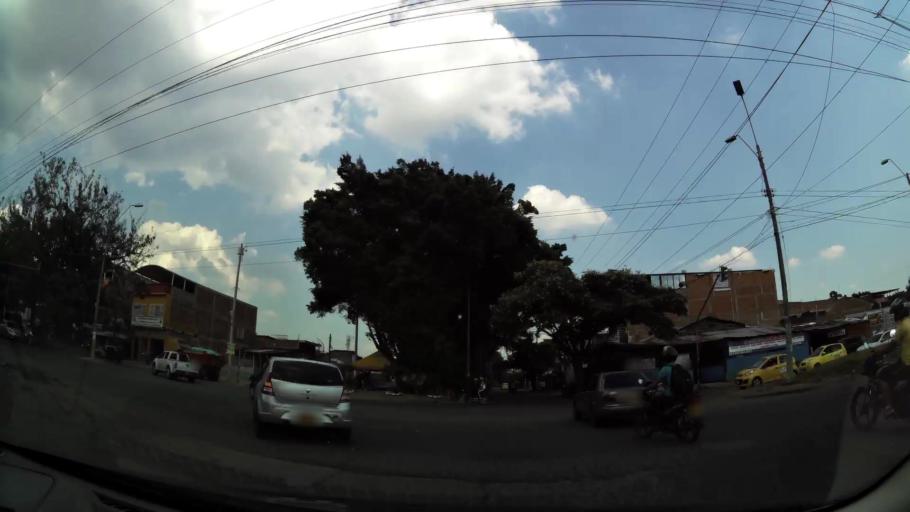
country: CO
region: Valle del Cauca
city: Cali
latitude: 3.4144
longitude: -76.5182
